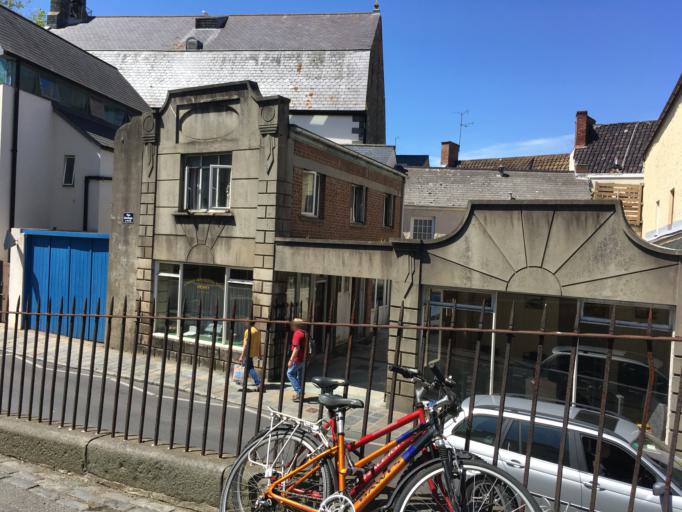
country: GG
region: St Peter Port
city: Saint Peter Port
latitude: 49.4522
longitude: -2.5401
